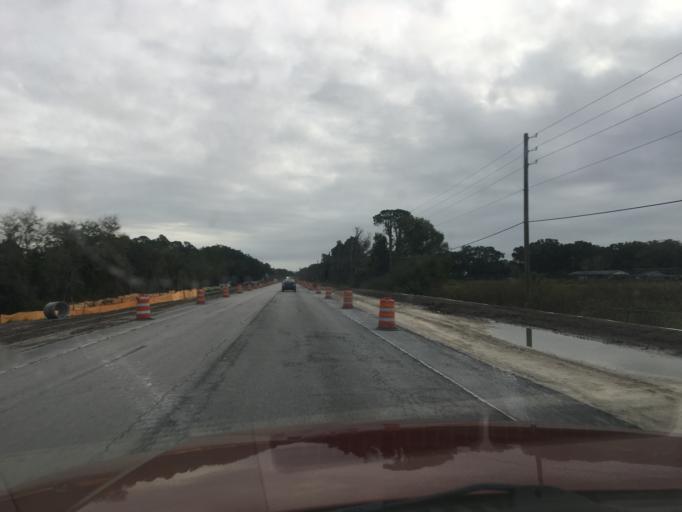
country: US
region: Florida
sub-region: Hillsborough County
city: Plant City
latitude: 28.0475
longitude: -82.1122
